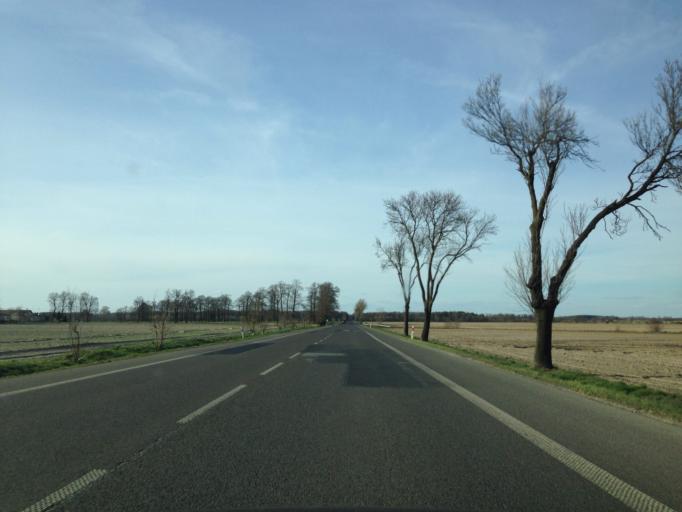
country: PL
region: Lodz Voivodeship
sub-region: Powiat kutnowski
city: Ostrowy
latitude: 52.3337
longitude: 19.1495
